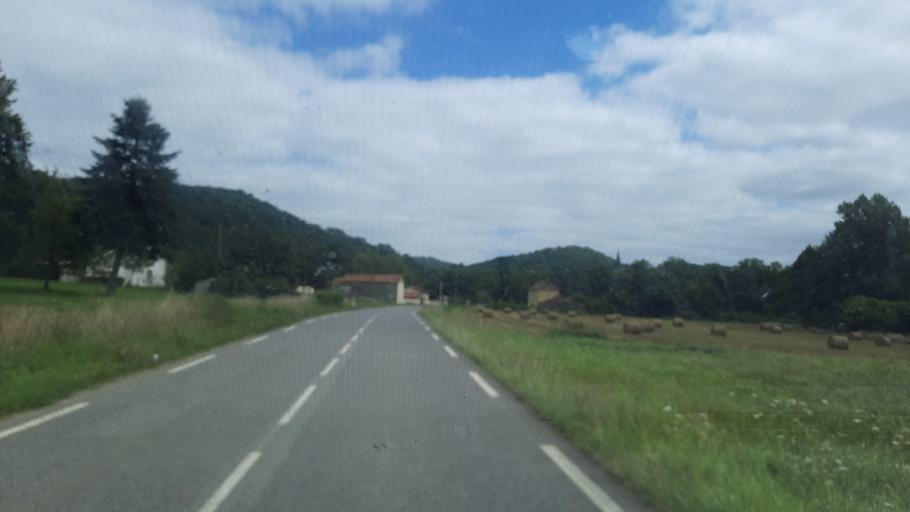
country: FR
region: Midi-Pyrenees
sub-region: Departement des Hautes-Pyrenees
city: Trie-sur-Baise
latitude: 43.3065
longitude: 0.2579
